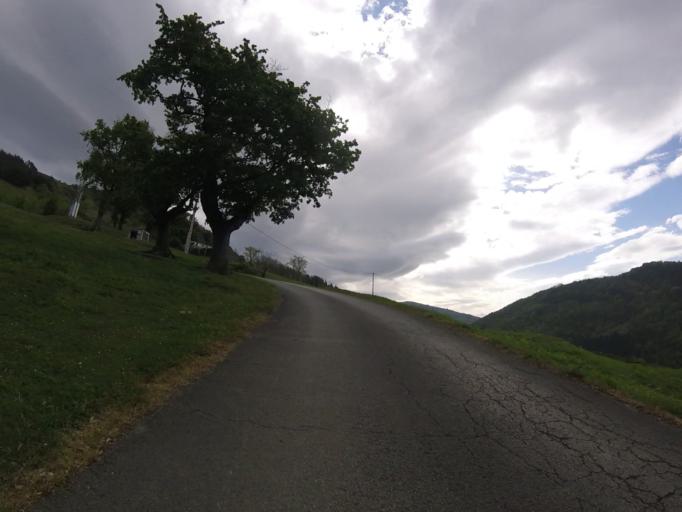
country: ES
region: Basque Country
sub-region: Provincia de Guipuzcoa
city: Aizarnazabal
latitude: 43.2546
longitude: -2.2273
